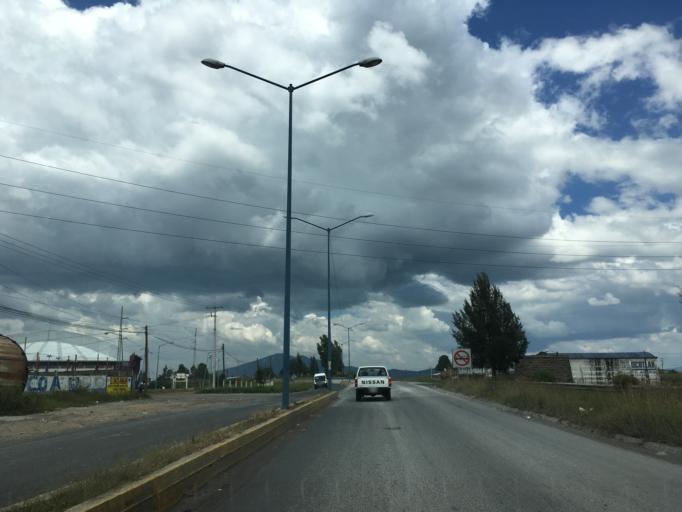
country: MX
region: Michoacan
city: Zacapu
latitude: 19.8386
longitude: -101.7683
